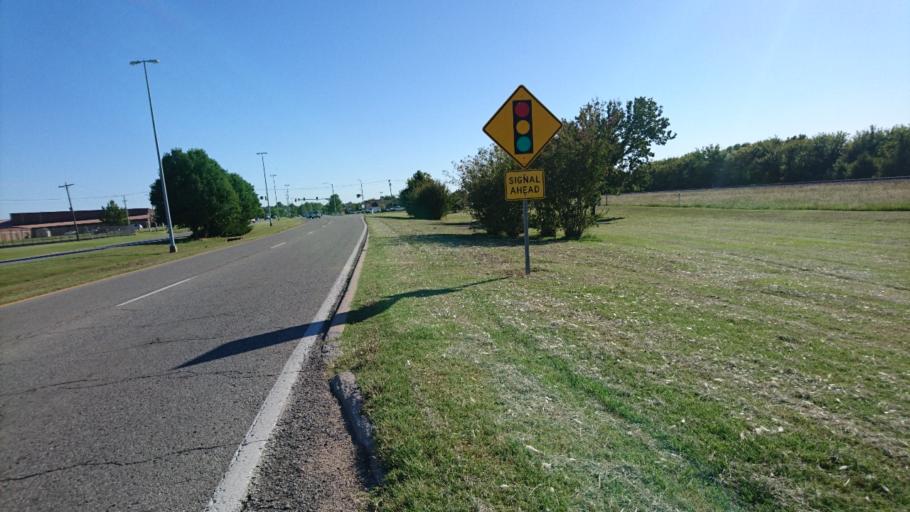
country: US
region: Oklahoma
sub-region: Rogers County
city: Claremore
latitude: 36.3307
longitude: -95.6058
